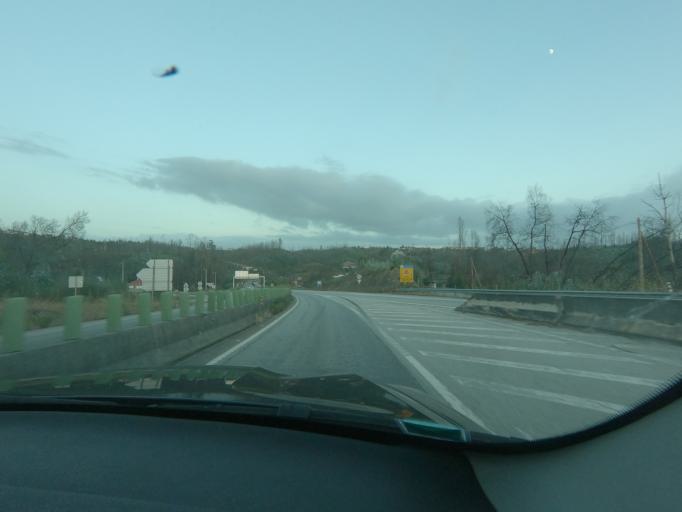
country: PT
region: Coimbra
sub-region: Penacova
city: Penacova
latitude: 40.3083
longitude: -8.2343
